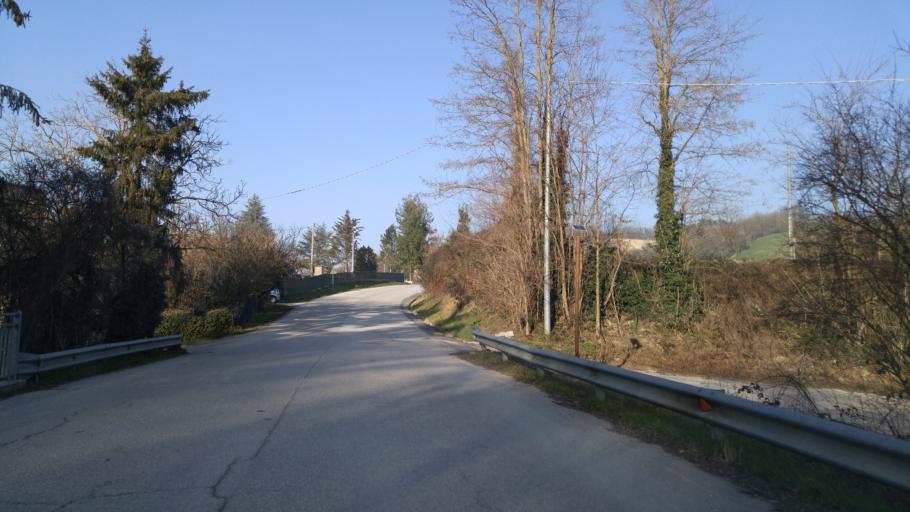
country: IT
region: The Marches
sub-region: Provincia di Pesaro e Urbino
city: Fenile
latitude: 43.8332
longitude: 12.9133
